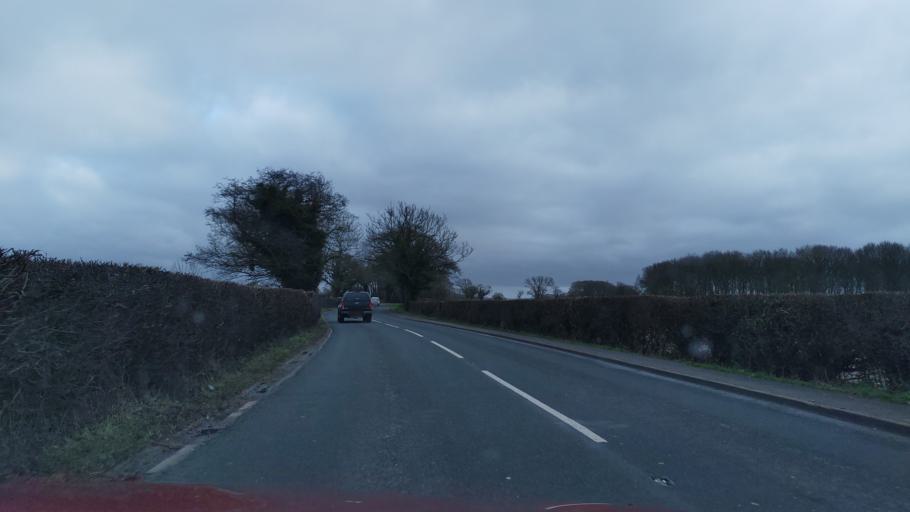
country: GB
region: England
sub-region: Lancashire
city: Tarleton
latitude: 53.6854
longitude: -2.8134
